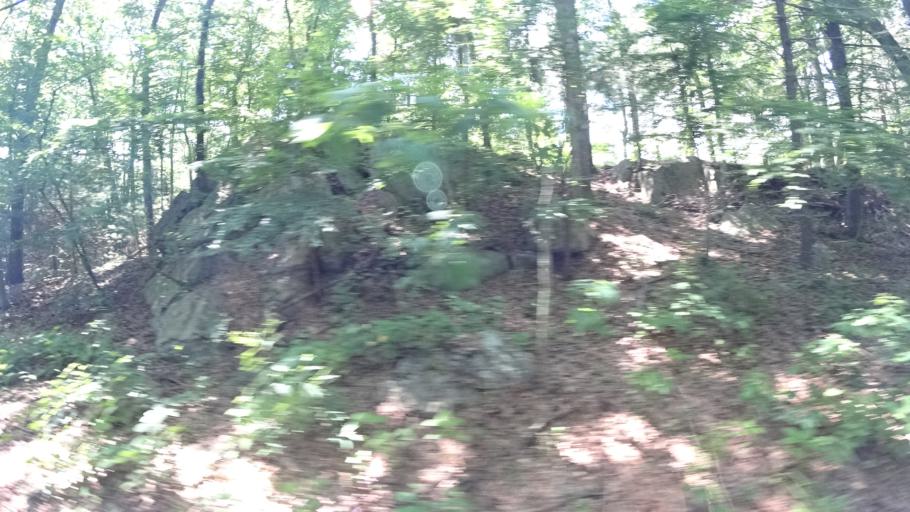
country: US
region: Massachusetts
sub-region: Norfolk County
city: Dedham
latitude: 42.2489
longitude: -71.1981
